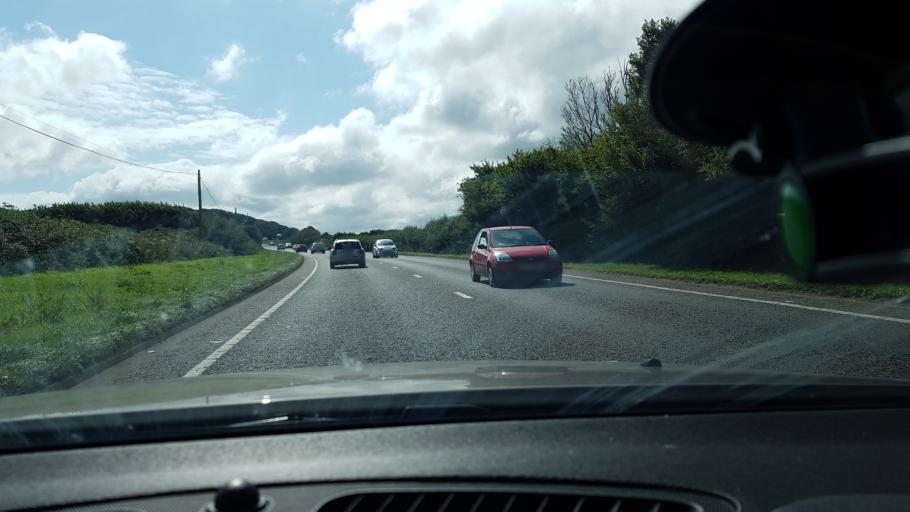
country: GB
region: England
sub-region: Cornwall
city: Truro
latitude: 50.3109
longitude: -5.0939
